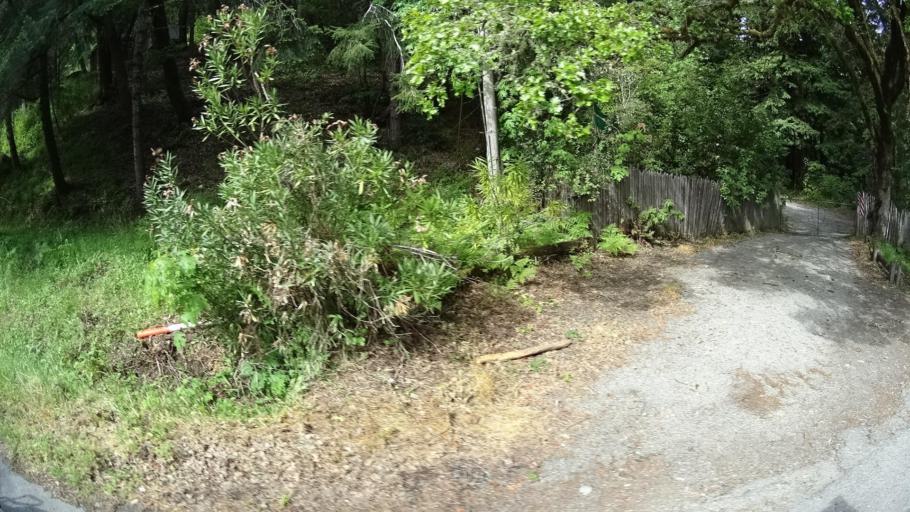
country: US
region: California
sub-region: Humboldt County
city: Redway
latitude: 40.0681
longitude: -123.8301
